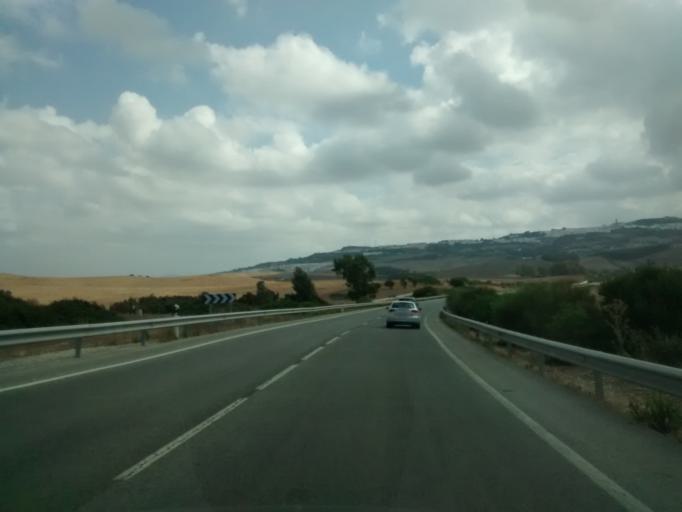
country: ES
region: Andalusia
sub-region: Provincia de Cadiz
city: Medina Sidonia
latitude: 36.4553
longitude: -5.9657
